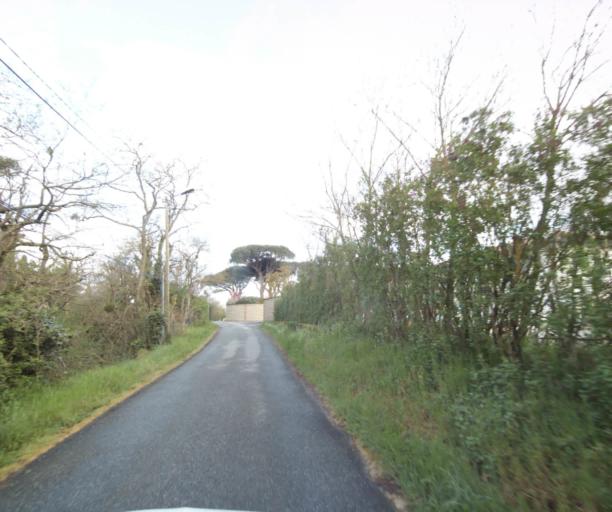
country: FR
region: Midi-Pyrenees
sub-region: Departement de l'Ariege
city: Saverdun
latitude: 43.2297
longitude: 1.5815
